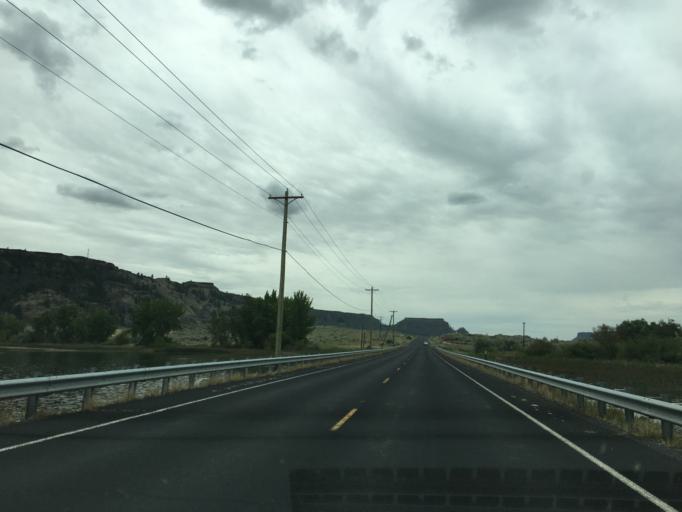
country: US
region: Washington
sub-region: Okanogan County
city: Coulee Dam
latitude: 47.9197
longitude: -119.0529
